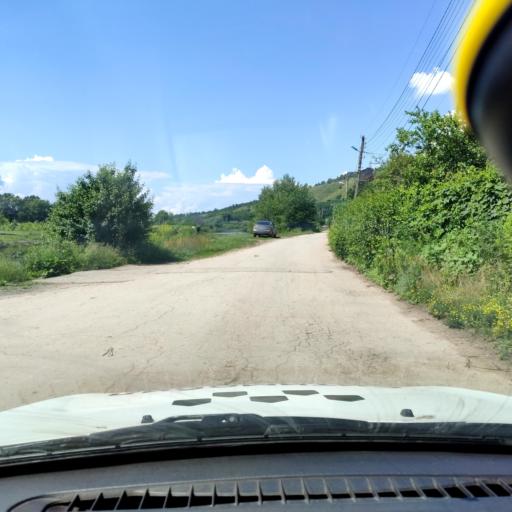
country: RU
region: Samara
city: Povolzhskiy
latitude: 53.4710
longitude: 49.6825
